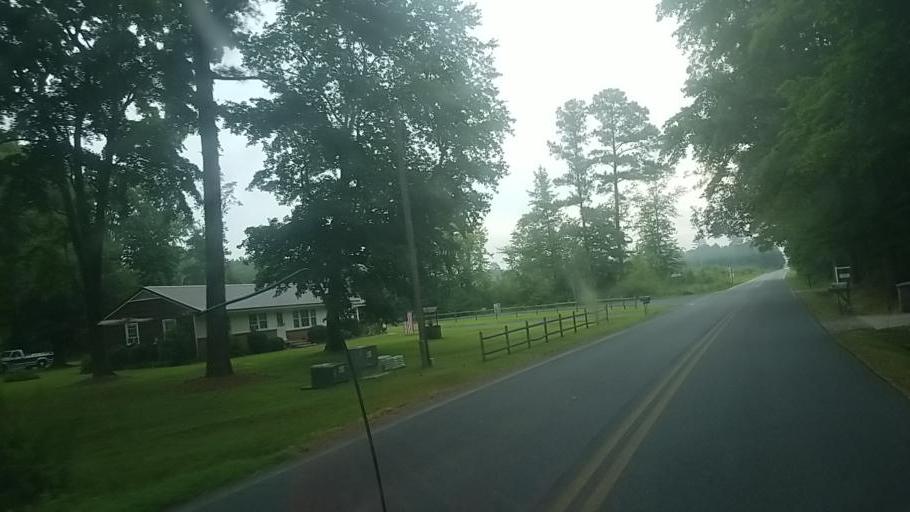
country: US
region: Maryland
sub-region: Wicomico County
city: Delmar
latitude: 38.4145
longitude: -75.5078
